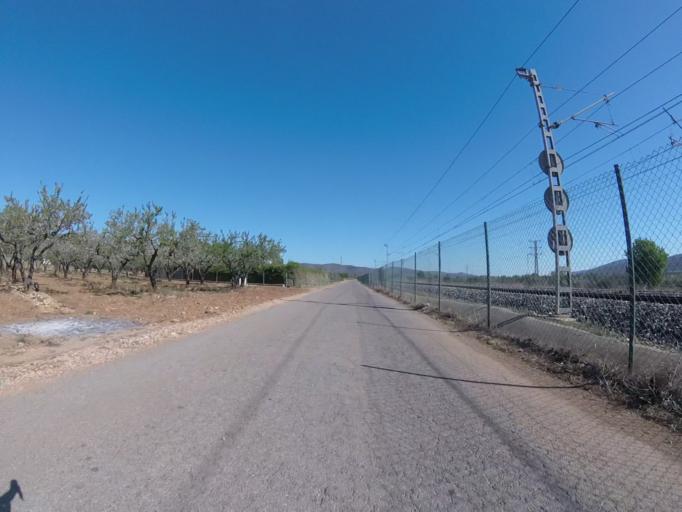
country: ES
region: Valencia
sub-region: Provincia de Castello
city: Alcala de Xivert
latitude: 40.3151
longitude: 0.2328
